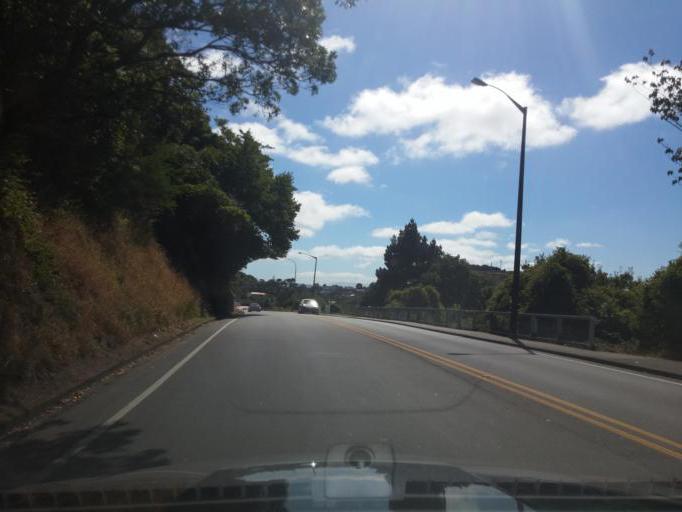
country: NZ
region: Wellington
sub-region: Wellington City
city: Wellington
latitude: -41.2383
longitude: 174.7975
